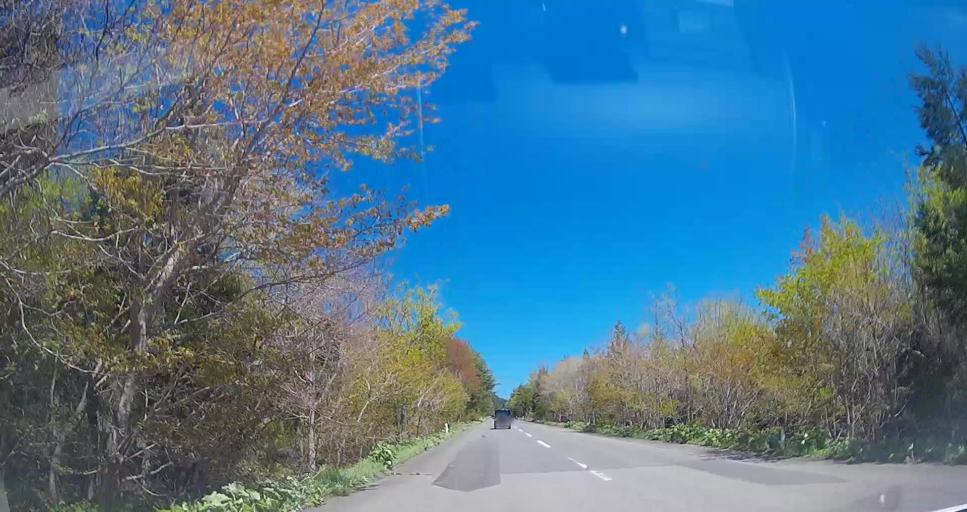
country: JP
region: Aomori
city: Mutsu
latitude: 41.3139
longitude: 141.3991
